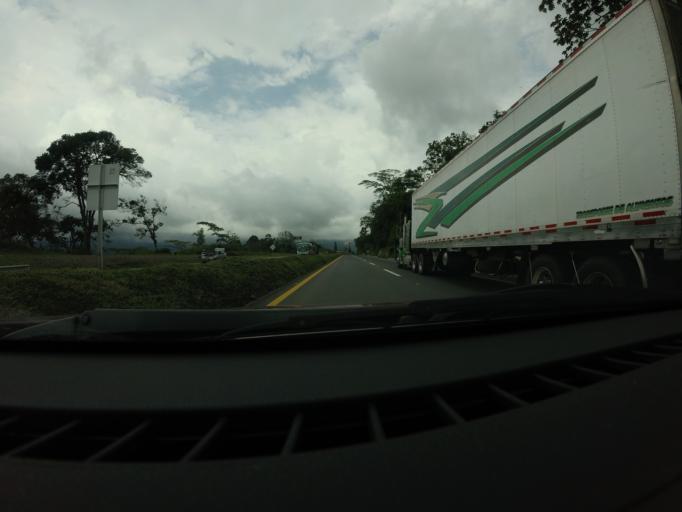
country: CO
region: Cundinamarca
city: San Francisco
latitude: 4.9640
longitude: -74.3061
